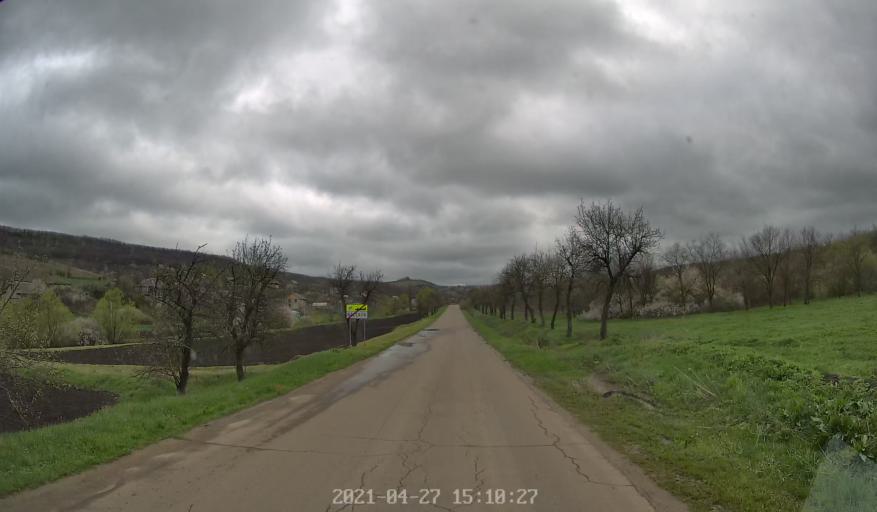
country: MD
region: Chisinau
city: Vadul lui Voda
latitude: 47.0404
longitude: 29.0327
